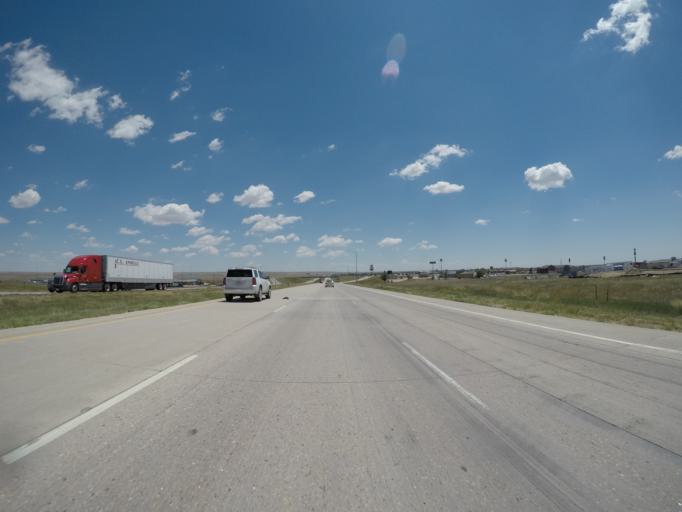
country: US
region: Colorado
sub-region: Lincoln County
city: Limon
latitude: 39.2731
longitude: -103.7136
